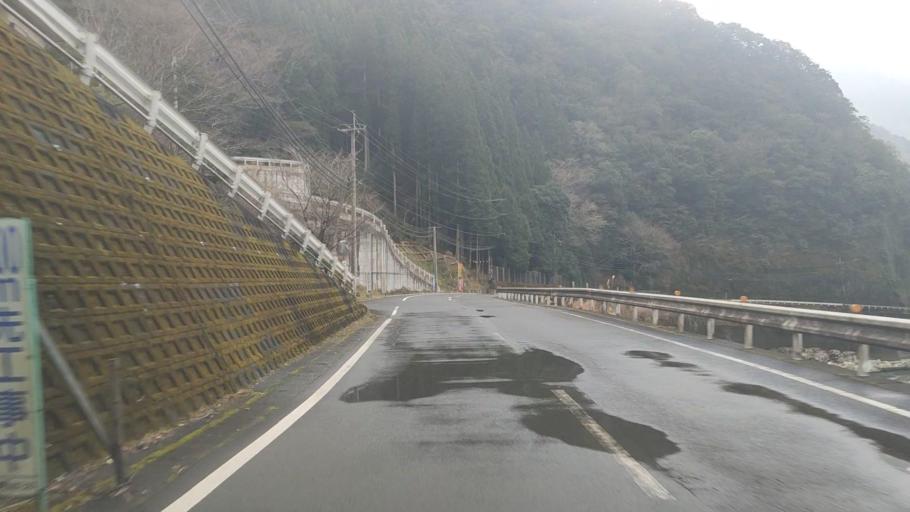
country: JP
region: Kumamoto
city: Hitoyoshi
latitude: 32.4261
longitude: 130.8569
